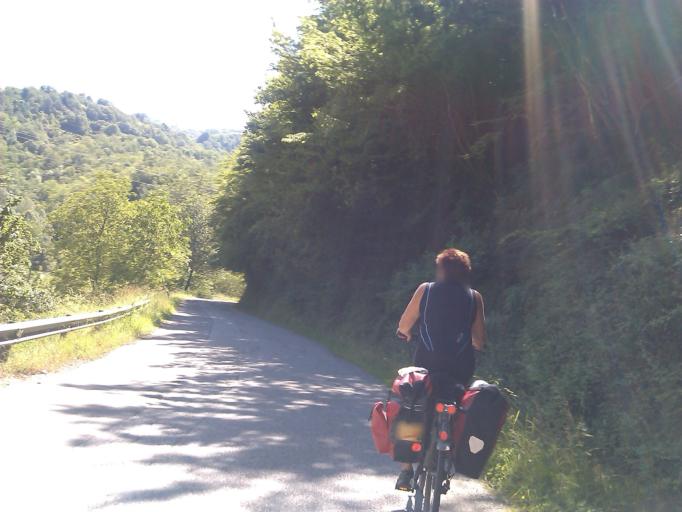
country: IT
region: Tuscany
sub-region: Provincia di Pistoia
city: Sambuca Pistoiese
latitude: 44.0769
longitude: 11.0513
